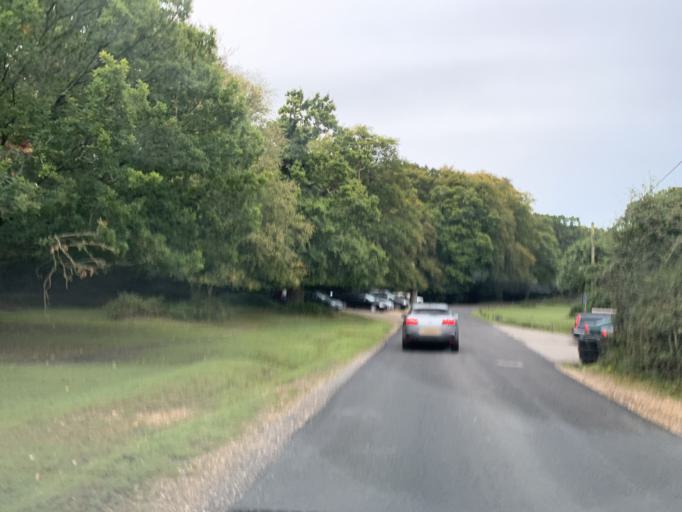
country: GB
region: England
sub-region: Wiltshire
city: Whiteparish
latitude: 50.9532
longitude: -1.6411
